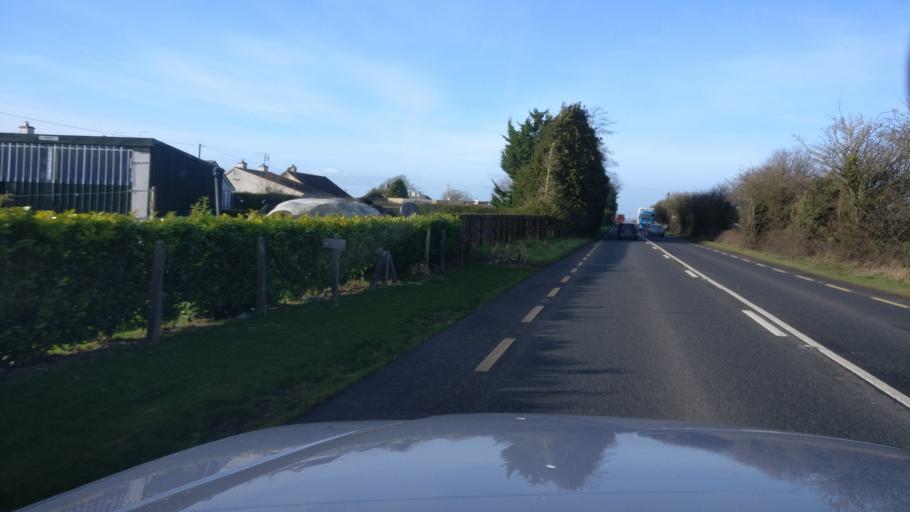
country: IE
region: Leinster
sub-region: Uibh Fhaili
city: Tullamore
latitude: 53.2066
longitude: -7.4355
